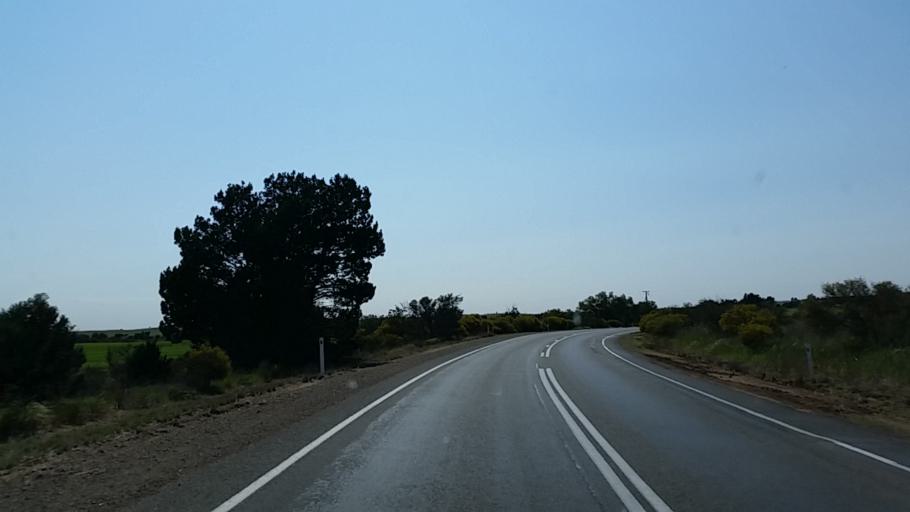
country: AU
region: South Australia
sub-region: Northern Areas
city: Jamestown
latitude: -33.2277
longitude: 138.3955
